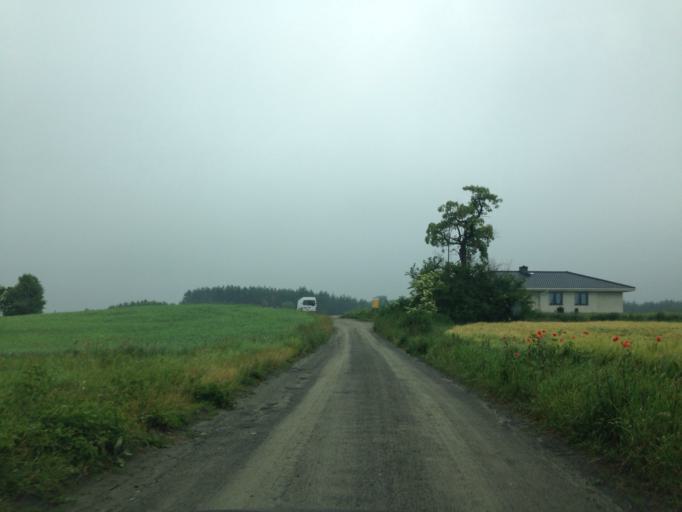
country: PL
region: Kujawsko-Pomorskie
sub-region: Powiat brodnicki
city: Brodnica
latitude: 53.3105
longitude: 19.3603
